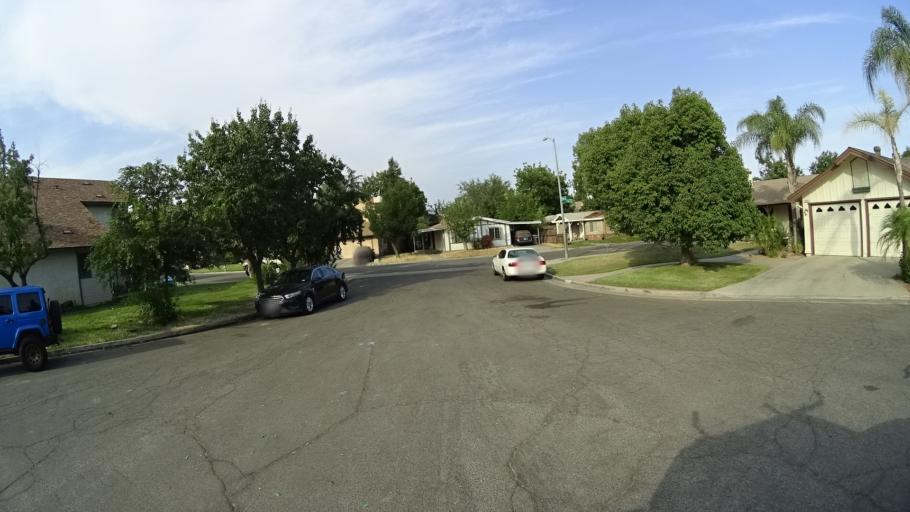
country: US
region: California
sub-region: Fresno County
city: West Park
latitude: 36.7711
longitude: -119.8493
